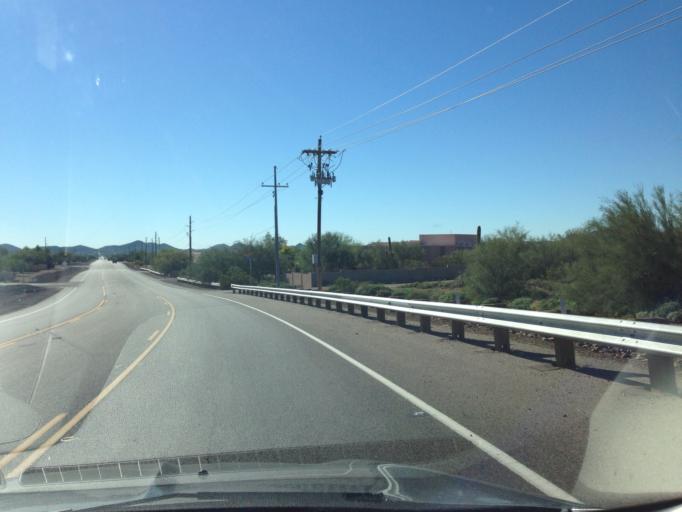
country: US
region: Arizona
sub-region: Maricopa County
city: Anthem
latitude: 33.8408
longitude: -112.0654
